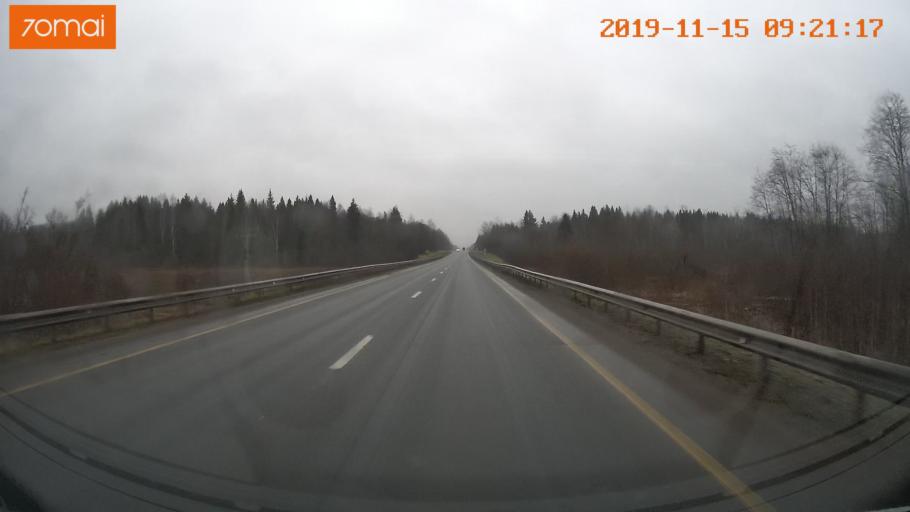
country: RU
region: Vologda
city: Tonshalovo
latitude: 59.2939
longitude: 38.0597
